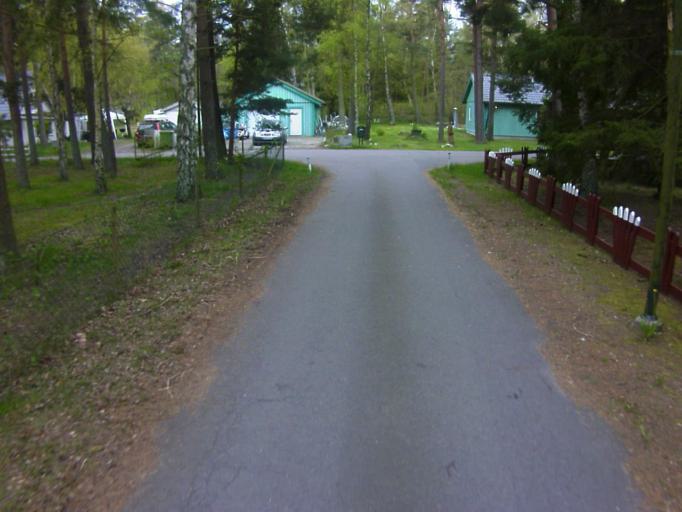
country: SE
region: Skane
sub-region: Kavlinge Kommun
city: Hofterup
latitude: 55.7619
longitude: 12.9848
